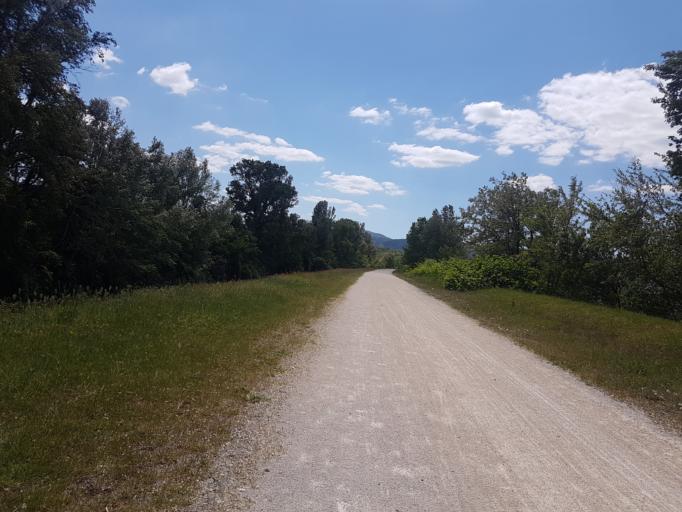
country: FR
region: Rhone-Alpes
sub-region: Departement de l'Ardeche
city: Mauves
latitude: 45.0480
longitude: 4.8578
